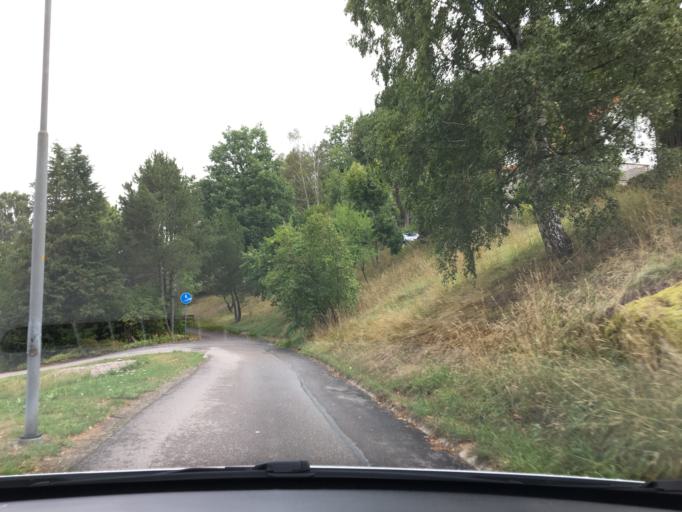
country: SE
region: Vaestra Goetaland
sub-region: Ale Kommun
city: Nodinge-Nol
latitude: 57.8938
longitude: 12.0622
